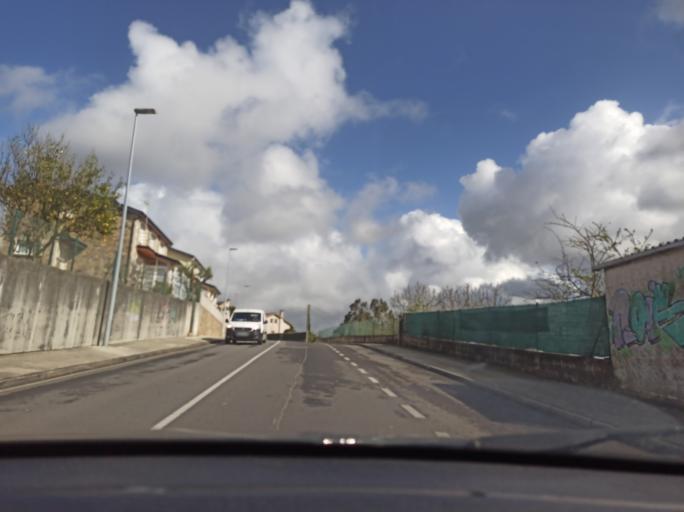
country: ES
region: Galicia
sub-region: Provincia da Coruna
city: Cambre
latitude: 43.3285
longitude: -8.3535
